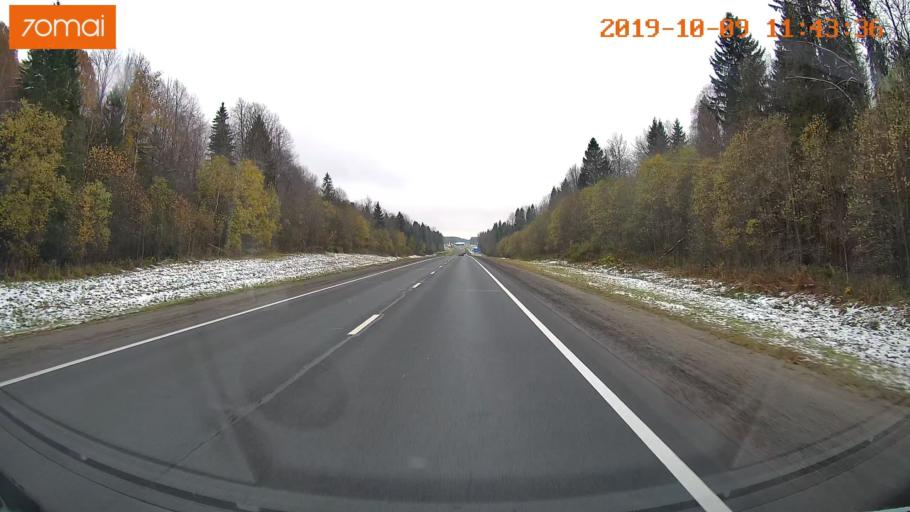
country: RU
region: Vologda
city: Gryazovets
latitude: 58.8944
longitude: 40.1866
